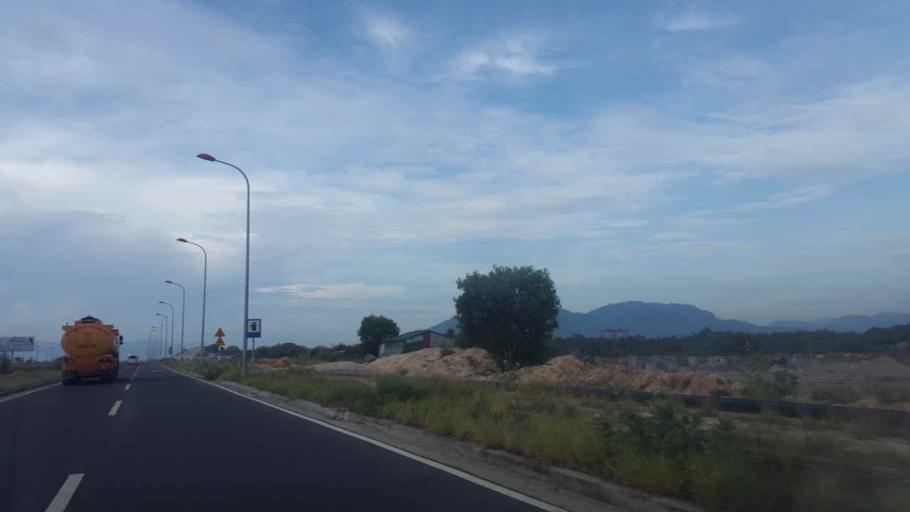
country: VN
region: Khanh Hoa
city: Cam Lam
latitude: 12.0139
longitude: 109.2123
